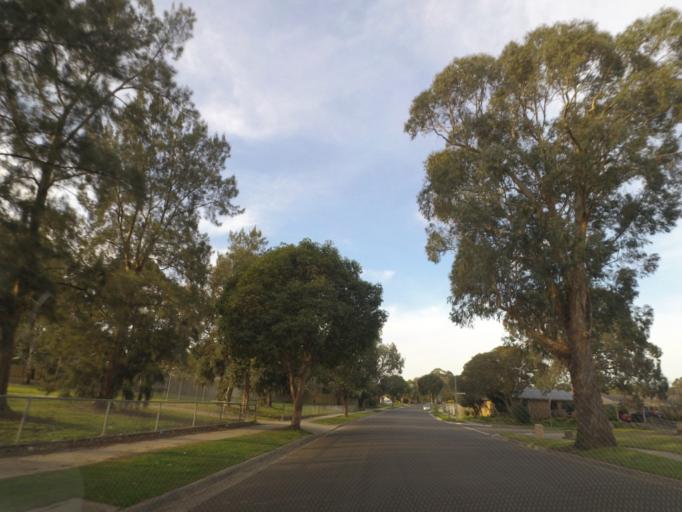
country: AU
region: Victoria
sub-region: Knox
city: Wantirna
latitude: -37.8570
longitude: 145.2325
